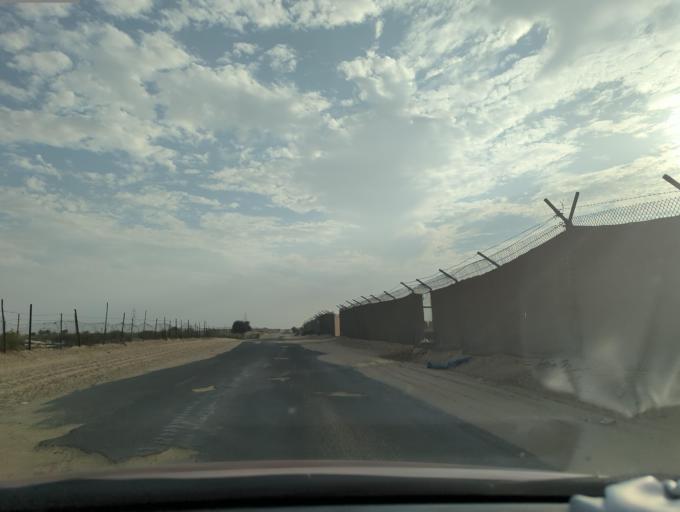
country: AE
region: Dubai
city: Dubai
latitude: 24.7198
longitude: 54.8663
